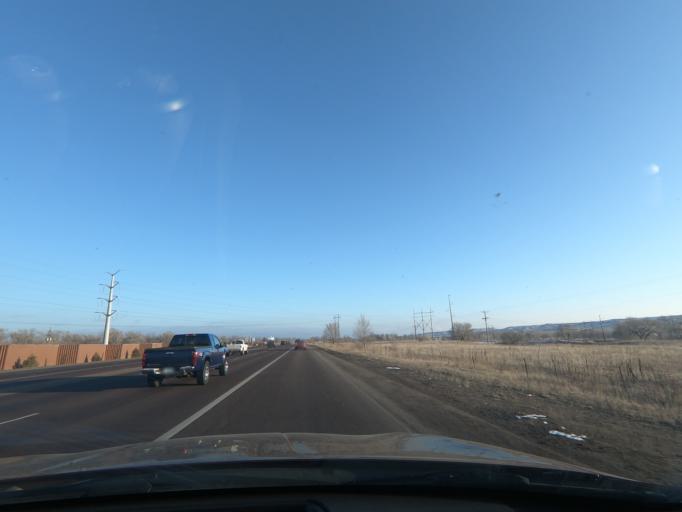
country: US
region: Colorado
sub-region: El Paso County
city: Stratmoor
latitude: 38.7665
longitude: -104.7592
